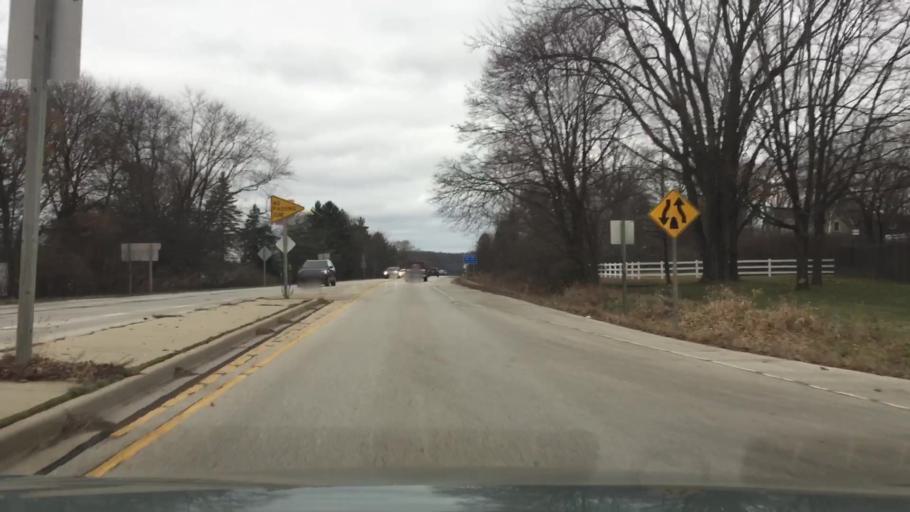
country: US
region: Wisconsin
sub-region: Waukesha County
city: Waukesha
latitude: 43.0213
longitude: -88.2702
